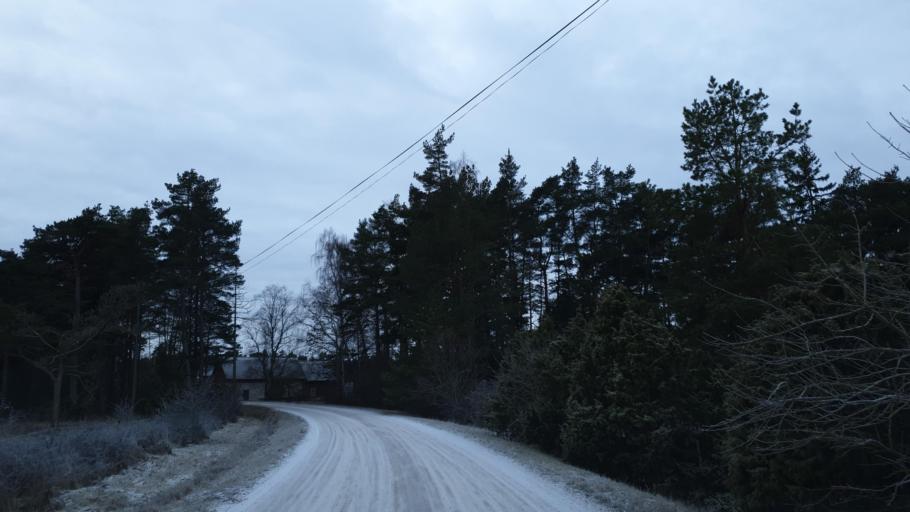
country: SE
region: Gotland
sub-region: Gotland
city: Slite
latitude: 57.4305
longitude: 18.8126
